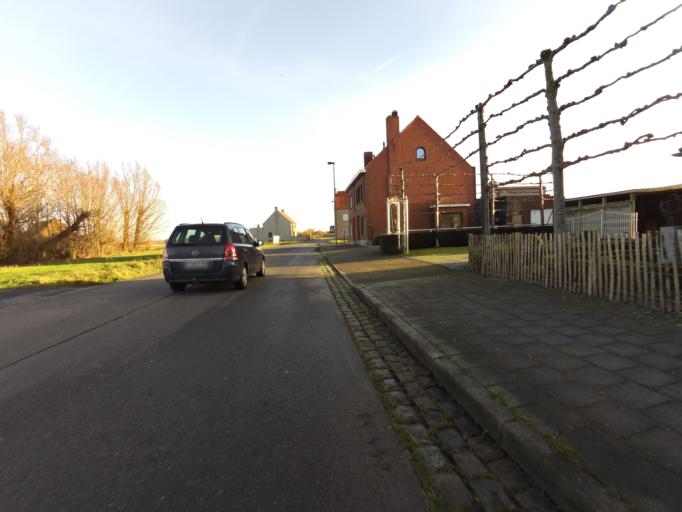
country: BE
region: Flanders
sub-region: Provincie West-Vlaanderen
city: Oudenburg
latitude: 51.1938
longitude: 2.9865
